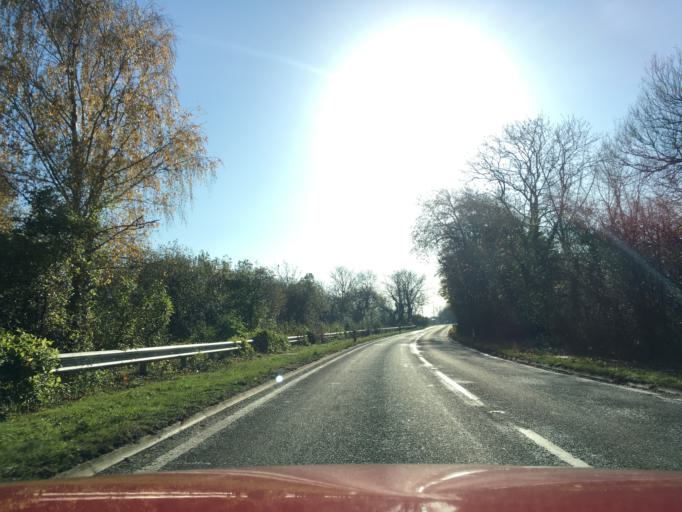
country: GB
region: England
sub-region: Somerset
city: Bridgwater
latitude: 51.1222
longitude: -2.9672
